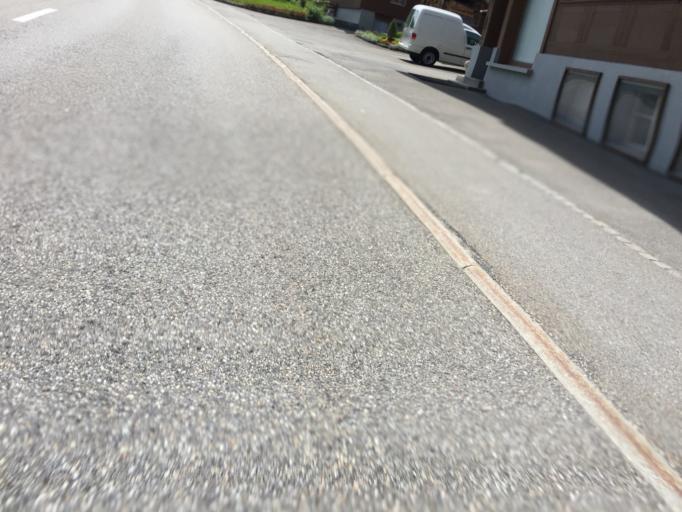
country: CH
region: Bern
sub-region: Emmental District
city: Trub
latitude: 46.9073
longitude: 7.8817
